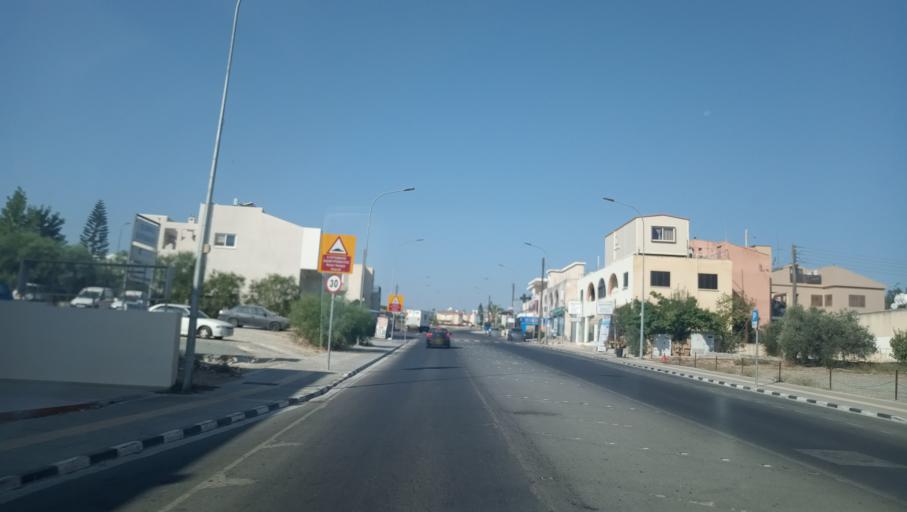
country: CY
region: Lefkosia
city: Geri
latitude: 35.1056
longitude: 33.4144
